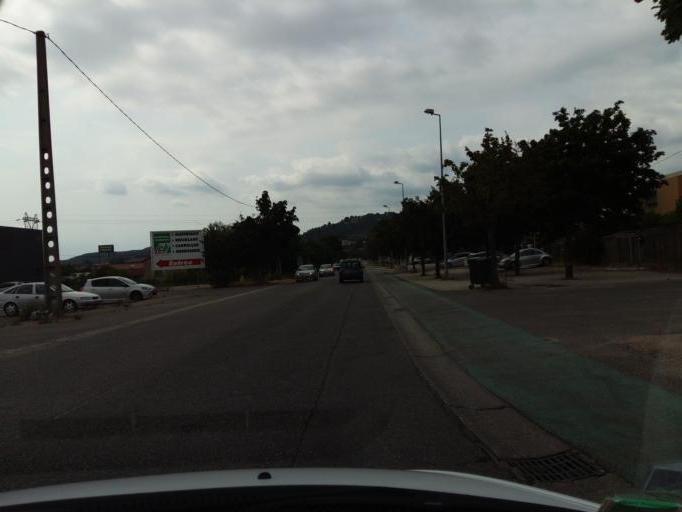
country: FR
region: Provence-Alpes-Cote d'Azur
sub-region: Departement du Vaucluse
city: Gargas
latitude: 43.8878
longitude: 5.3754
